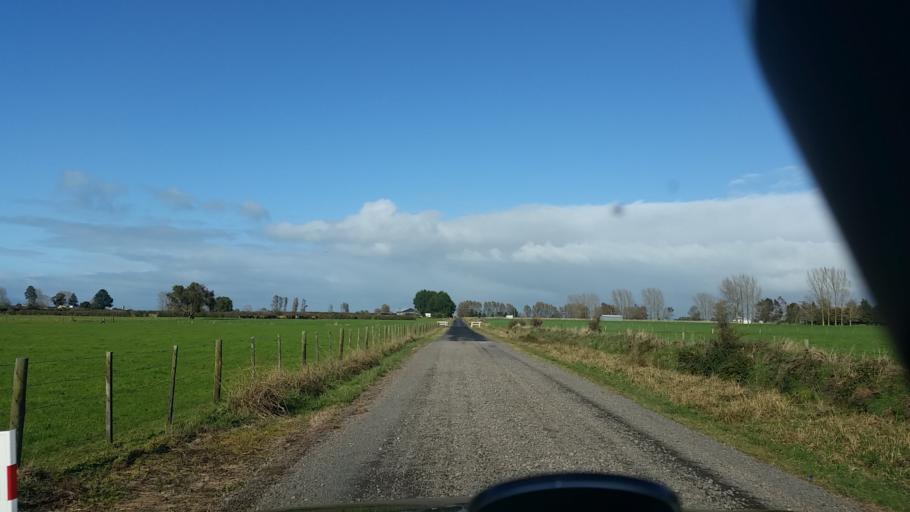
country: NZ
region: Bay of Plenty
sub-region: Western Bay of Plenty District
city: Katikati
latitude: -37.5924
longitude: 175.7132
